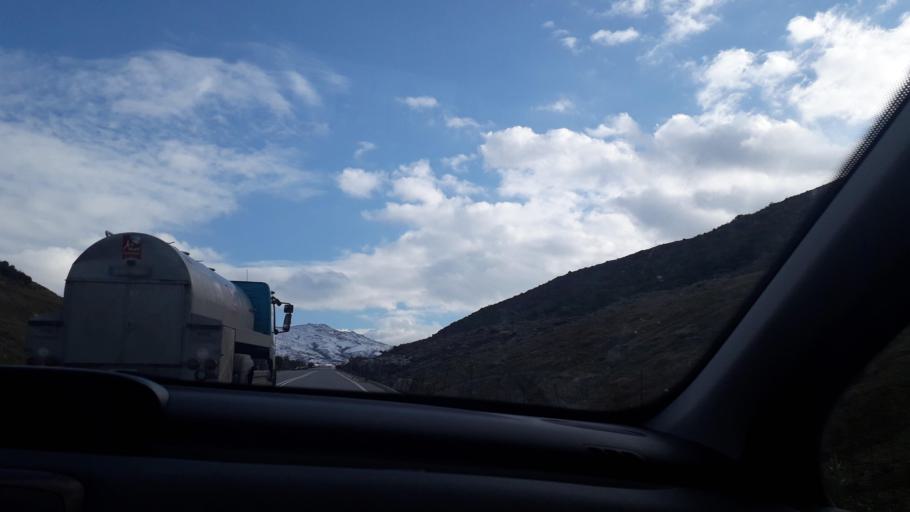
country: GR
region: Crete
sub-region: Nomos Rethymnis
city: Agia Foteini
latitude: 35.2720
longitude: 24.5618
